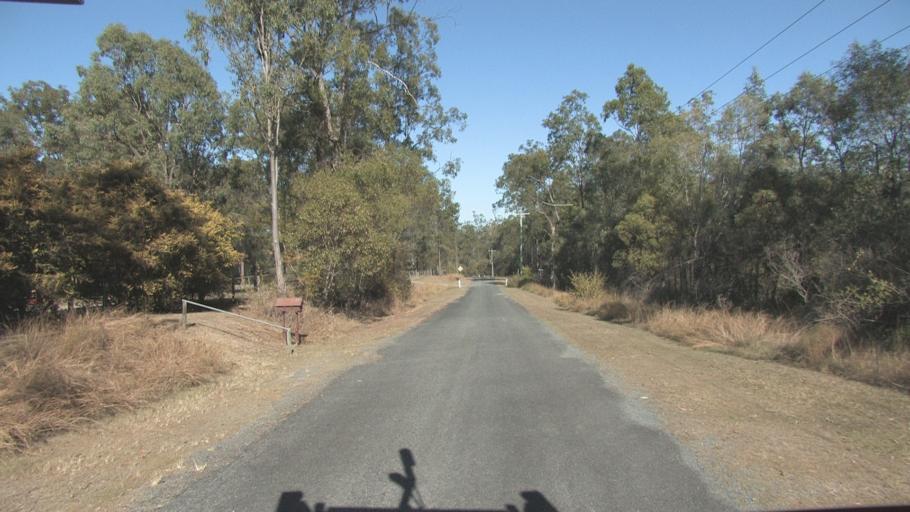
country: AU
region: Queensland
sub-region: Logan
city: Cedar Vale
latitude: -27.8462
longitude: 153.0584
